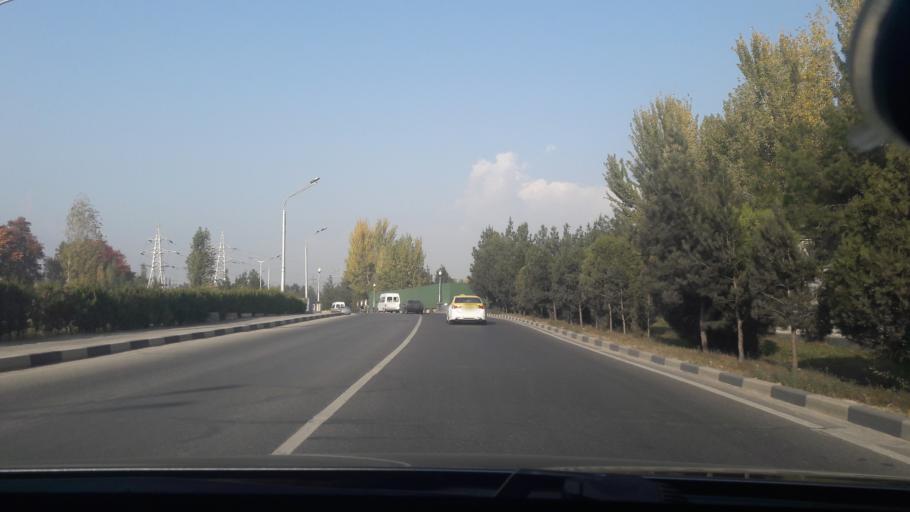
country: TJ
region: Dushanbe
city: Dushanbe
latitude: 38.5793
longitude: 68.7730
